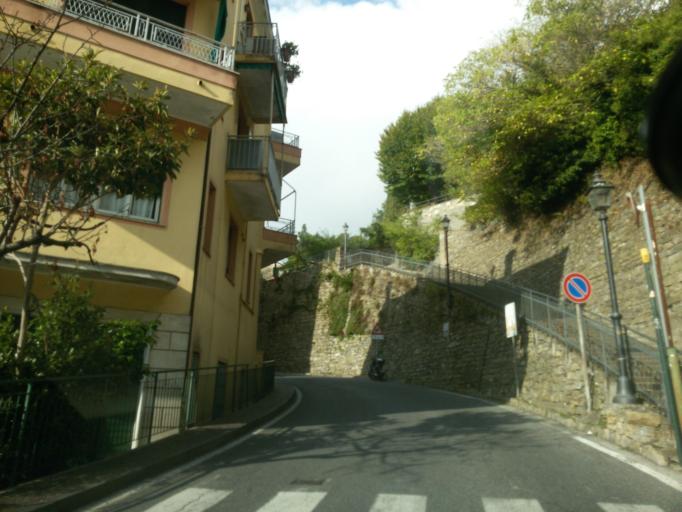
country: IT
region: Liguria
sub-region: Provincia di Genova
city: Camogli
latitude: 44.3441
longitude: 9.1707
